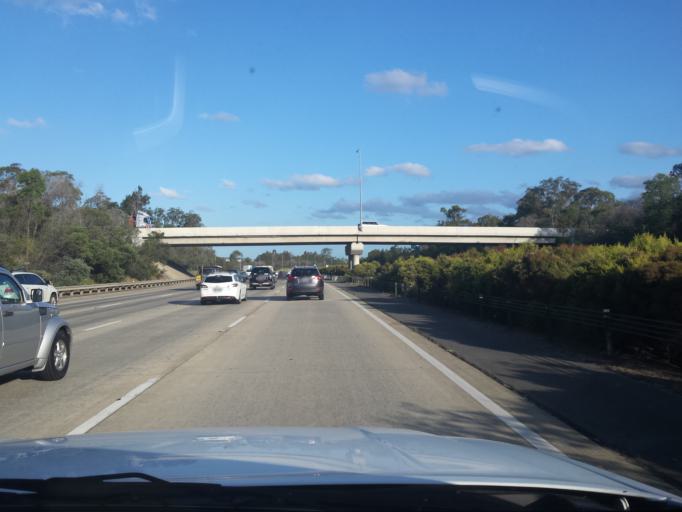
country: AU
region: Queensland
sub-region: Gold Coast
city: Ormeau Hills
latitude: -27.7576
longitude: 153.2415
